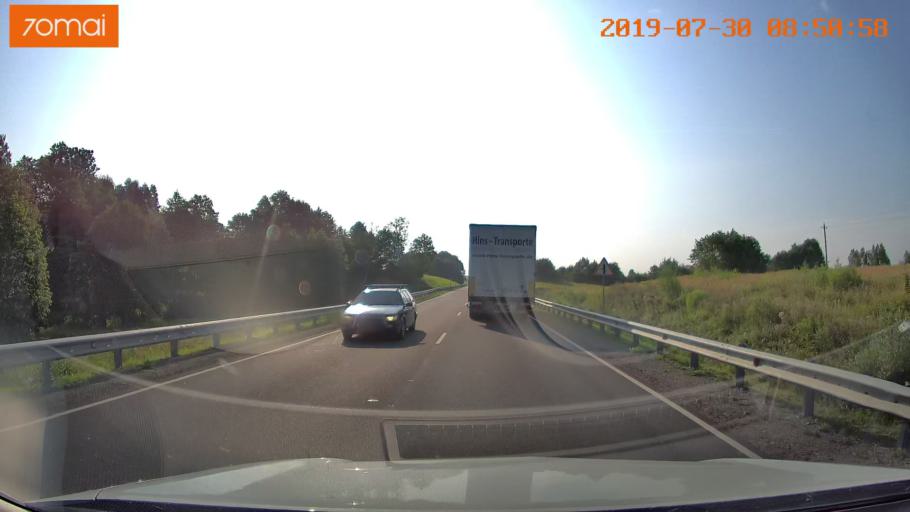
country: RU
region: Kaliningrad
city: Chernyakhovsk
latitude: 54.6046
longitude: 21.9491
